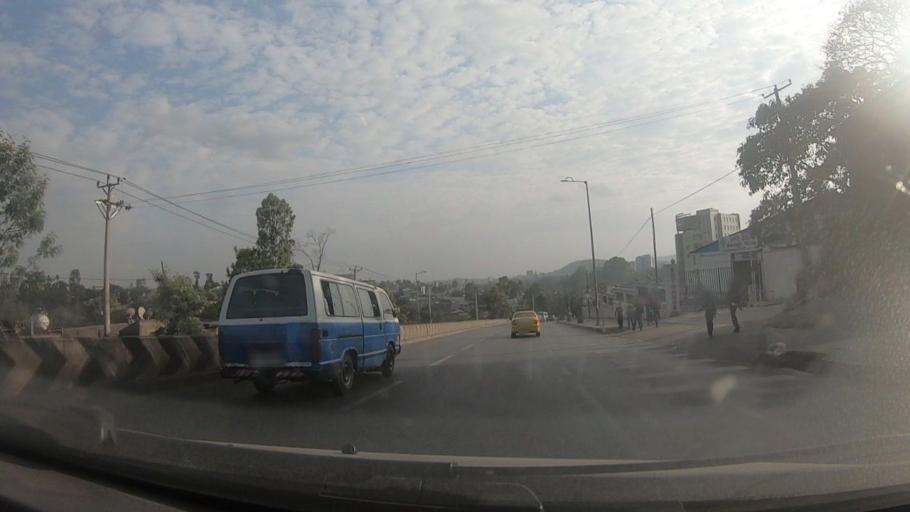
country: ET
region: Adis Abeba
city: Addis Ababa
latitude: 8.9772
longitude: 38.7341
